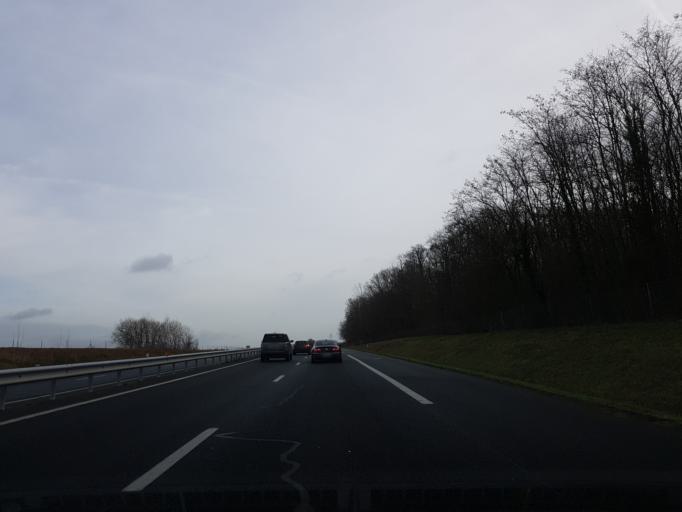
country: FR
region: Bourgogne
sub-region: Departement de l'Yonne
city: Thorigny-sur-Oreuse
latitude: 48.2350
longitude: 3.4208
